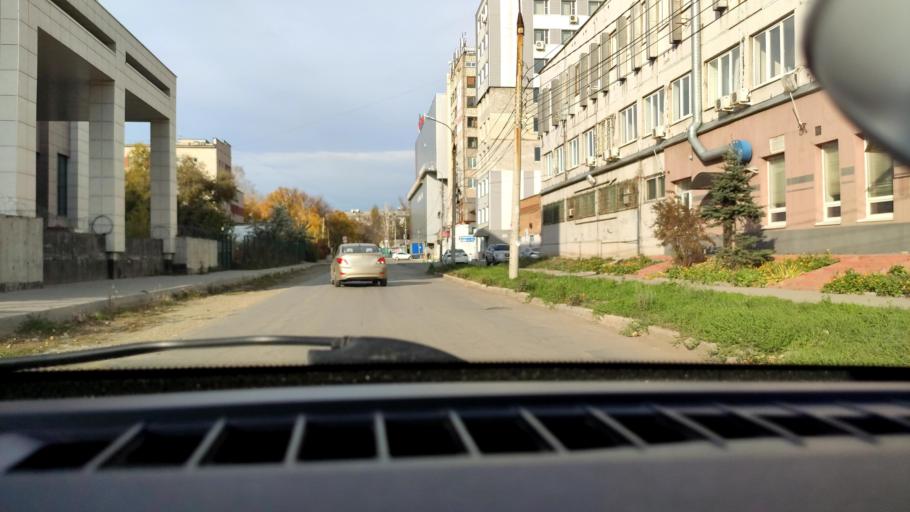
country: RU
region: Samara
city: Samara
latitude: 53.1896
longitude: 50.1874
